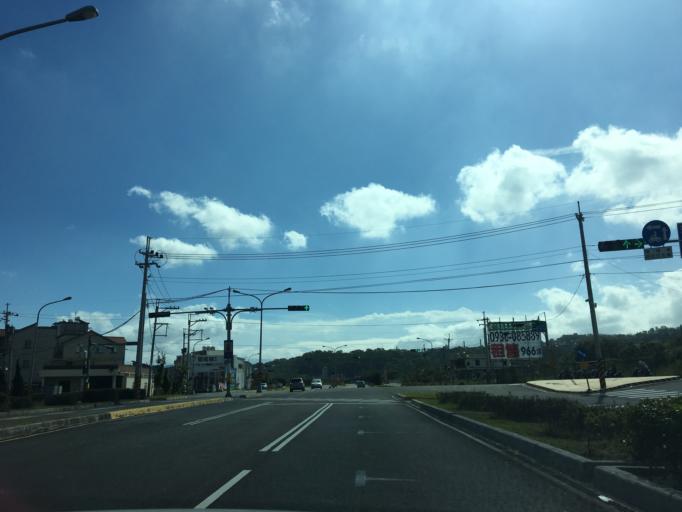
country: TW
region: Taiwan
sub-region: Hsinchu
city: Zhubei
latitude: 24.7837
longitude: 121.0377
